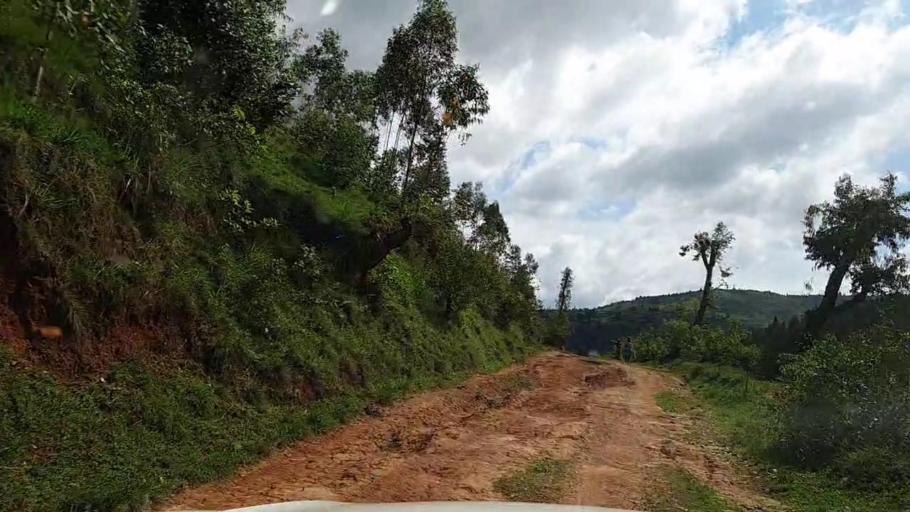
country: RW
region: Southern Province
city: Gikongoro
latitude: -2.3854
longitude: 29.5481
